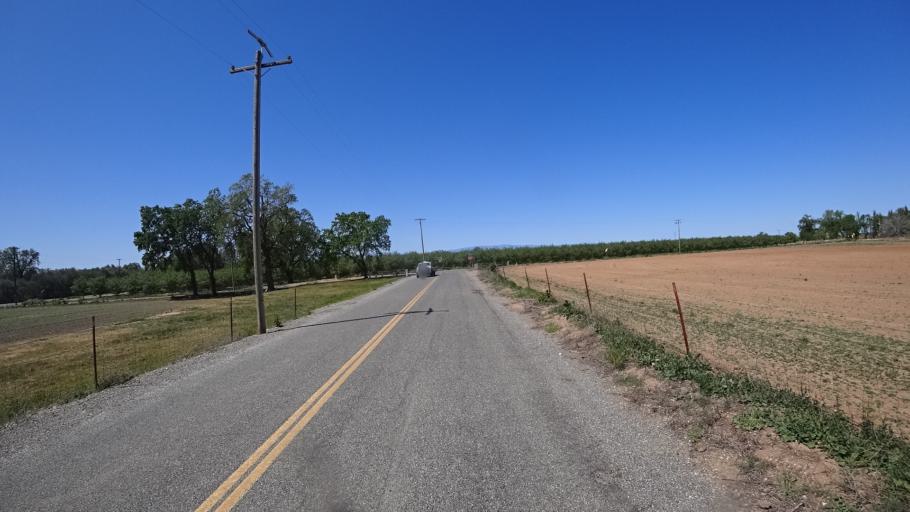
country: US
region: California
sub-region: Glenn County
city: Orland
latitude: 39.7921
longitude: -122.2292
